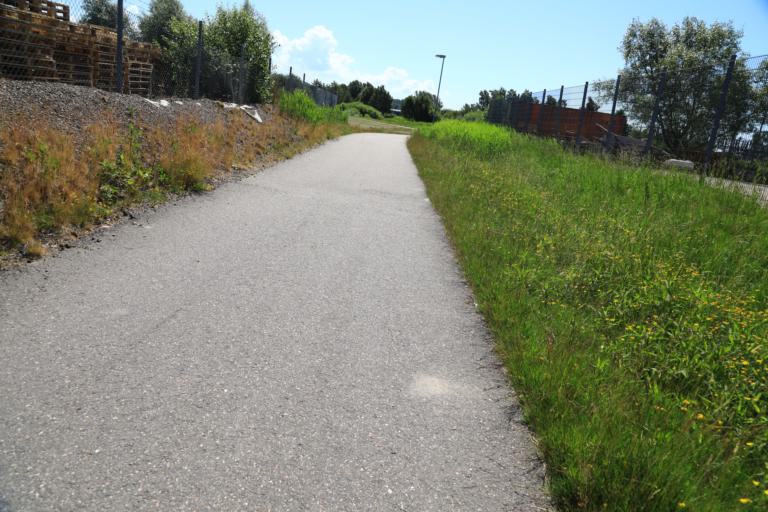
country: SE
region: Halland
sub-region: Kungsbacka Kommun
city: Kungsbacka
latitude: 57.5079
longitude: 12.0702
